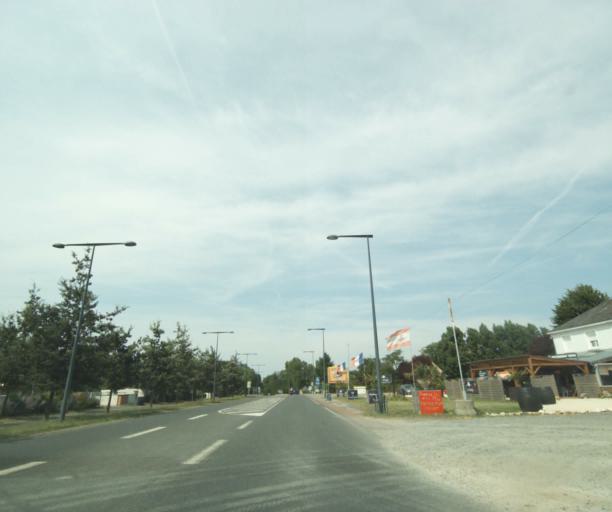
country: FR
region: Centre
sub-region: Departement d'Indre-et-Loire
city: Montbazon
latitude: 47.2782
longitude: 0.7105
